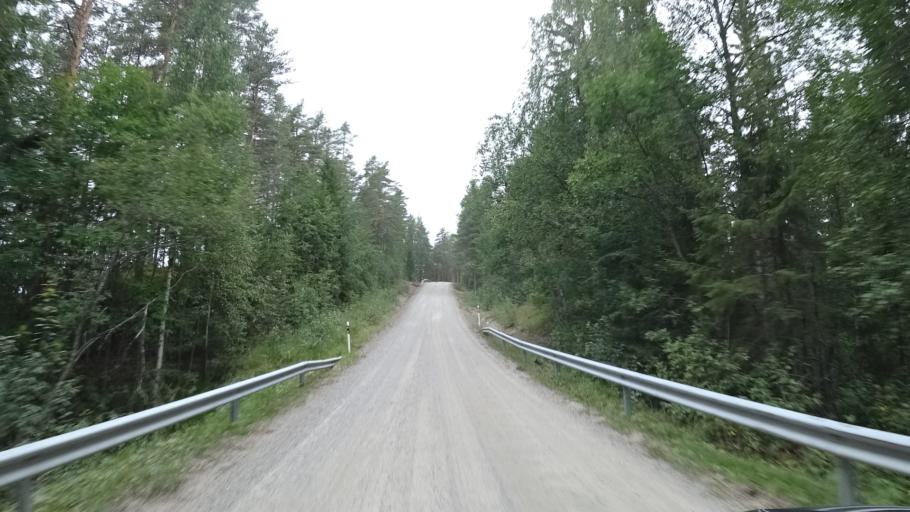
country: FI
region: North Karelia
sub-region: Pielisen Karjala
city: Lieksa
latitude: 63.2324
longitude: 30.3701
